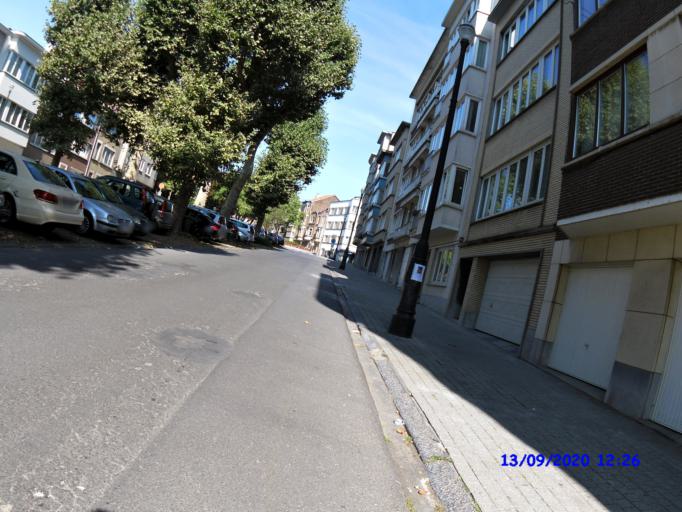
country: BE
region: Brussels Capital
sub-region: Bruxelles-Capitale
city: Brussels
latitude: 50.8614
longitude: 4.3231
